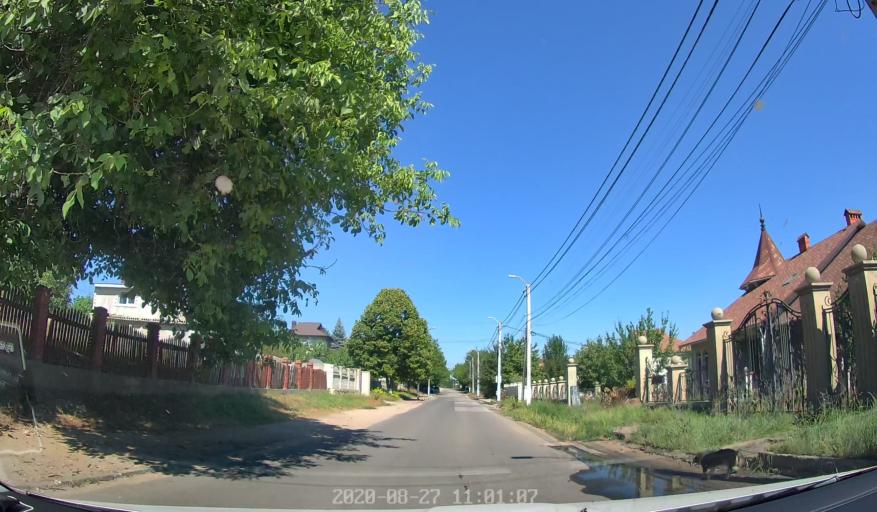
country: MD
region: Laloveni
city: Ialoveni
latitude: 46.9593
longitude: 28.7572
